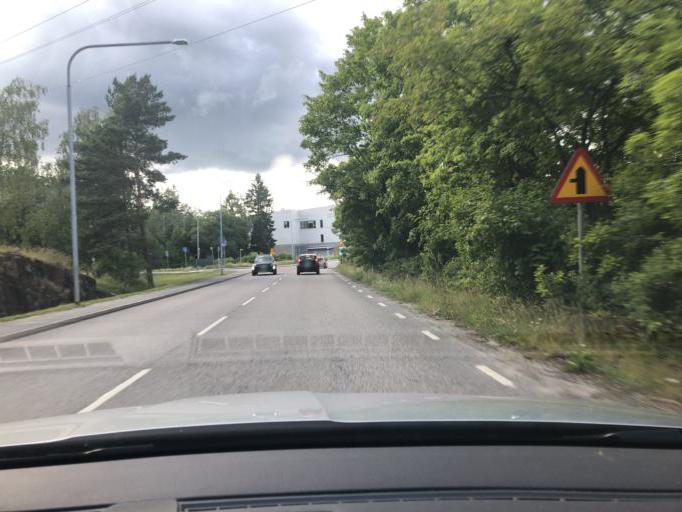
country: SE
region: Stockholm
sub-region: Botkyrka Kommun
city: Tullinge
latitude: 59.2244
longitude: 17.9330
